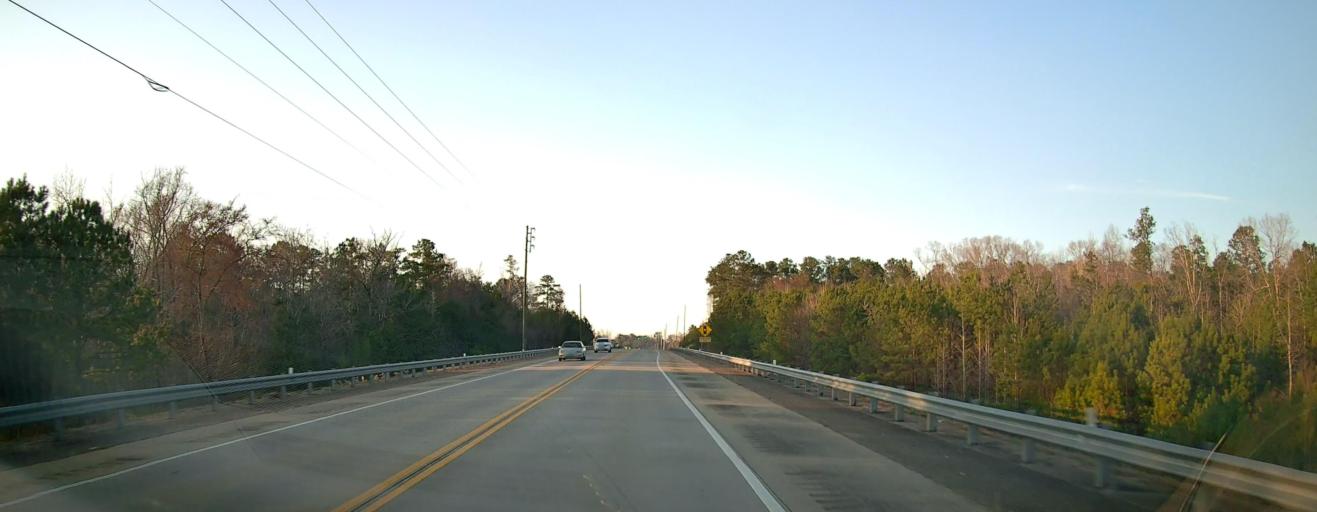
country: US
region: Georgia
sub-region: Troup County
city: La Grange
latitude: 33.0032
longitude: -85.0858
